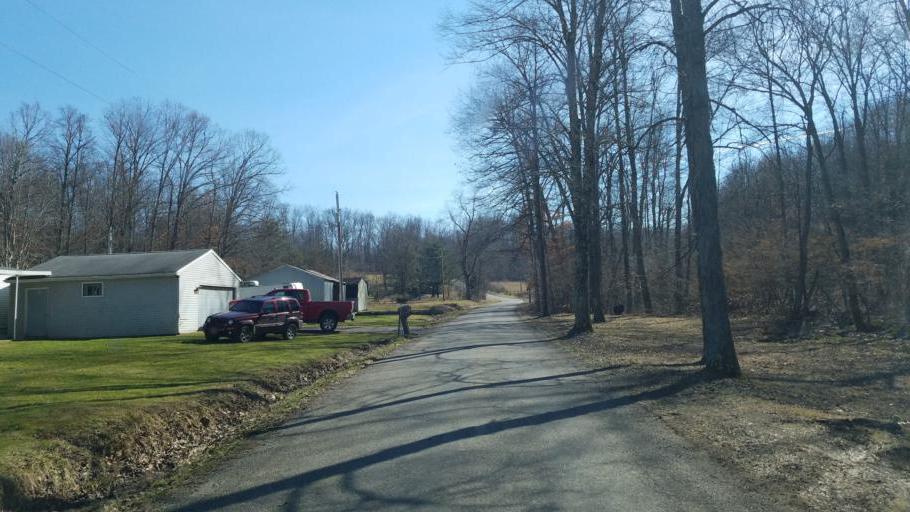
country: US
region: Ohio
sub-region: Ashland County
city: Loudonville
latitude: 40.5770
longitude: -82.3209
